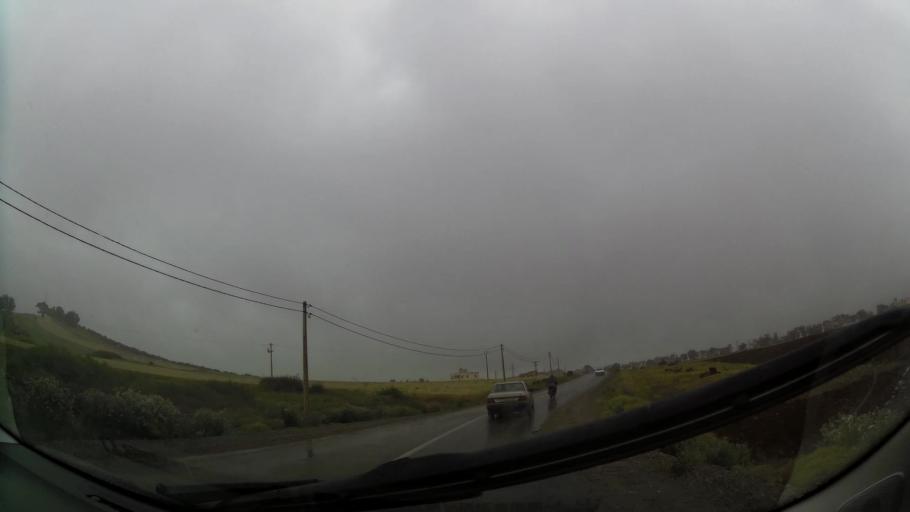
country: MA
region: Oriental
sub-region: Nador
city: Boudinar
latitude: 35.1343
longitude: -3.6238
